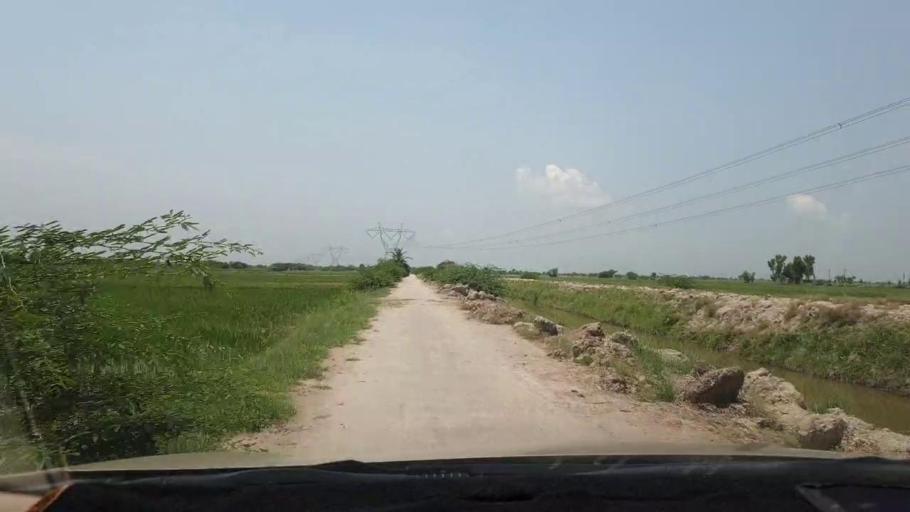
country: PK
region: Sindh
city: Naudero
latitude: 27.6654
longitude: 68.2794
